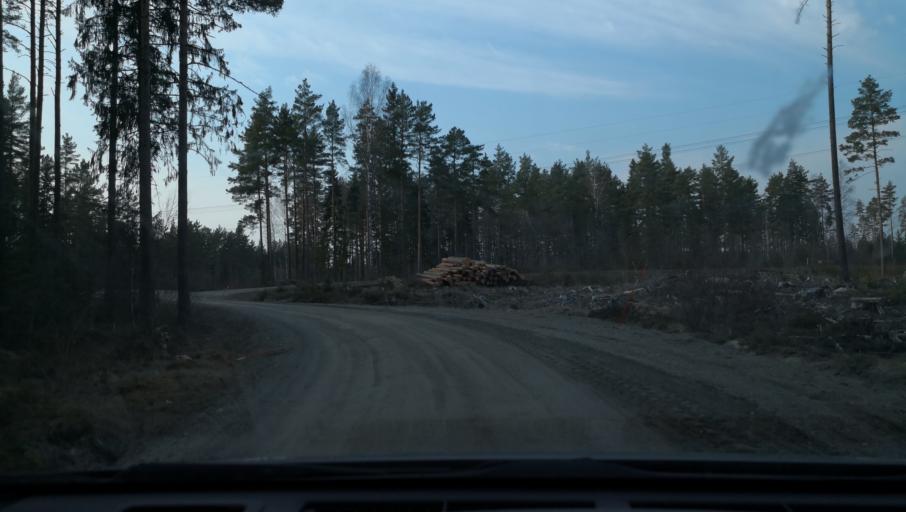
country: SE
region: OErebro
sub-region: Lindesbergs Kommun
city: Frovi
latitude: 59.3677
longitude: 15.3251
